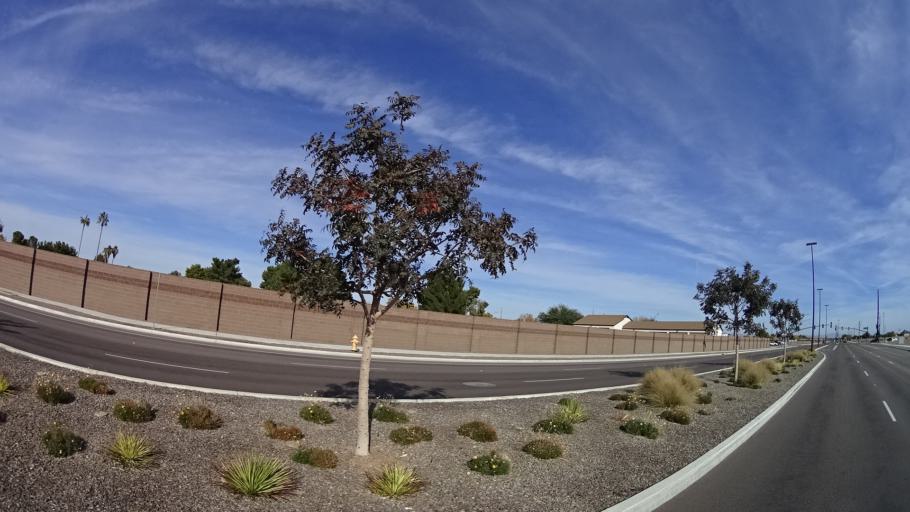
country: US
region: Arizona
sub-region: Maricopa County
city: Gilbert
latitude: 33.2778
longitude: -111.7399
